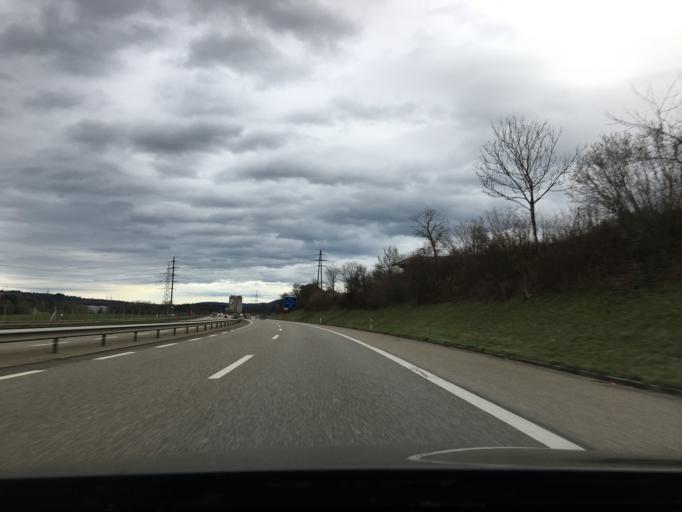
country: CH
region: Aargau
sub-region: Bezirk Rheinfelden
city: Stein
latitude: 47.5407
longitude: 7.9708
